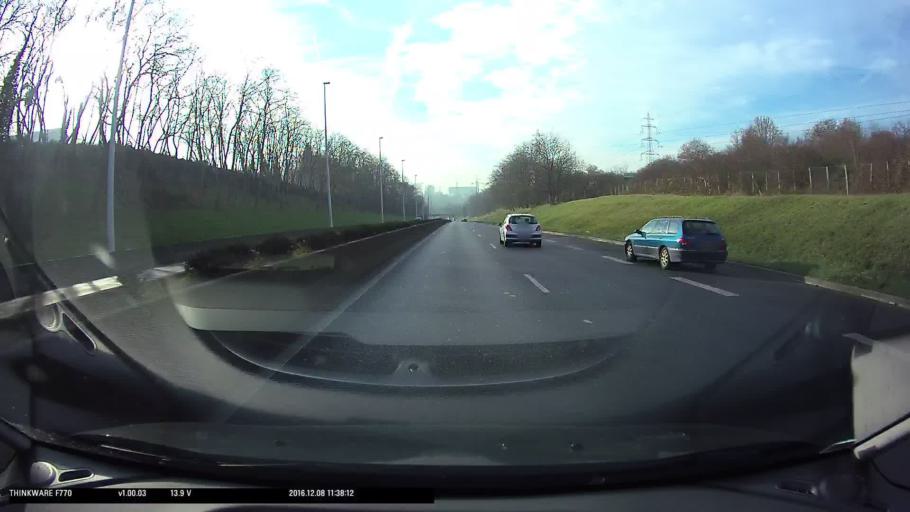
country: FR
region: Ile-de-France
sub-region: Departement du Val-d'Oise
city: Pontoise
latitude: 49.0608
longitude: 2.0845
